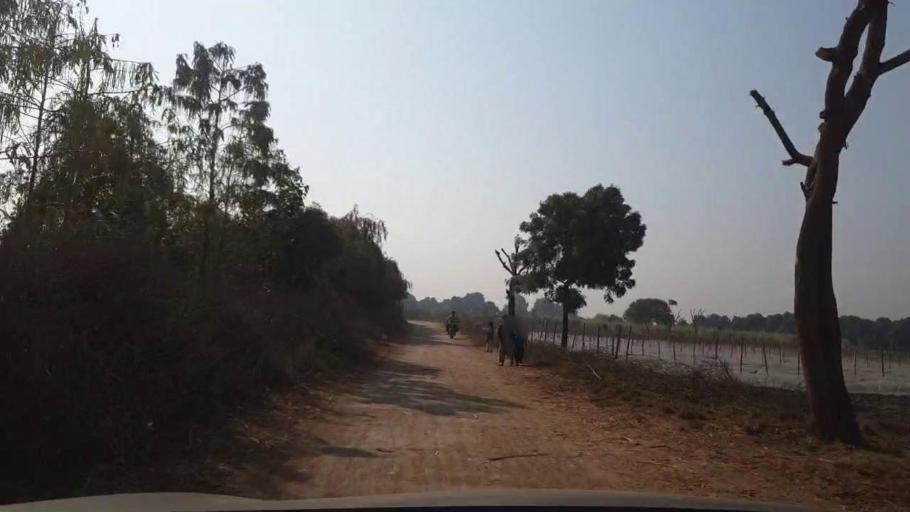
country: PK
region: Sindh
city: Tando Allahyar
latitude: 25.4841
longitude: 68.7562
